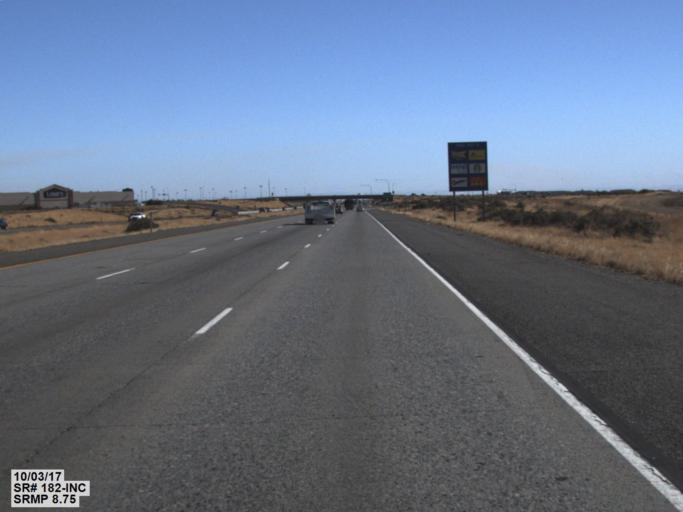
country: US
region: Washington
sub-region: Franklin County
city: West Pasco
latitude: 46.2689
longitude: -119.1935
